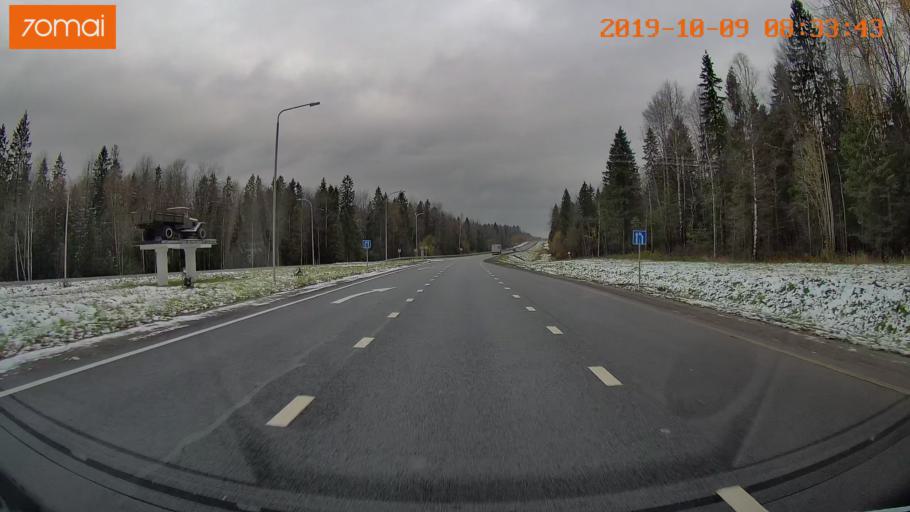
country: RU
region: Vologda
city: Gryazovets
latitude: 58.8863
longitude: 40.1908
